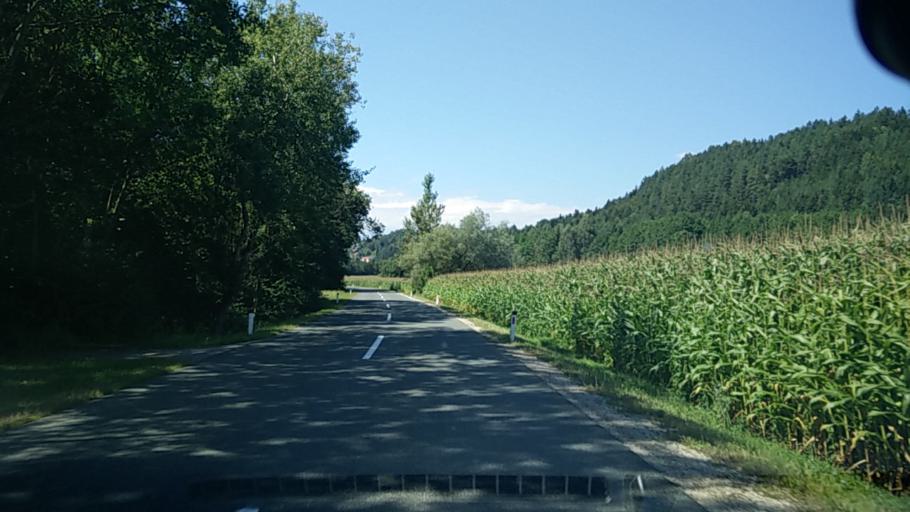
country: AT
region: Carinthia
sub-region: Politischer Bezirk Volkermarkt
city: Sittersdorf
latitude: 46.5540
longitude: 14.5771
